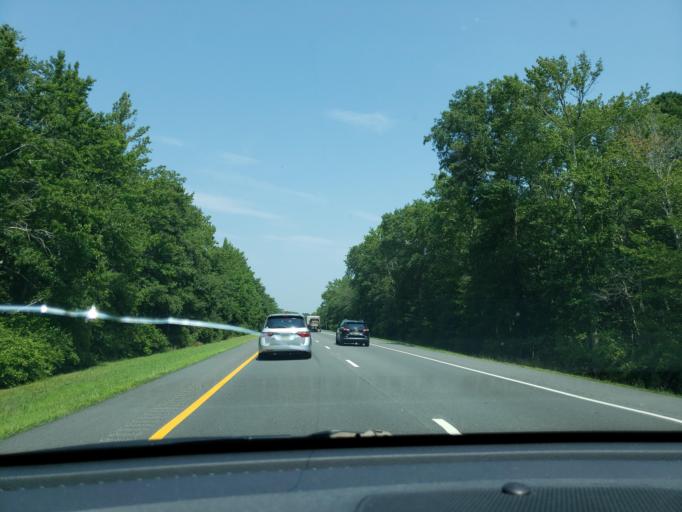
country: US
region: New Jersey
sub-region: Cape May County
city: Avalon
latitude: 39.1386
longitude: -74.7627
